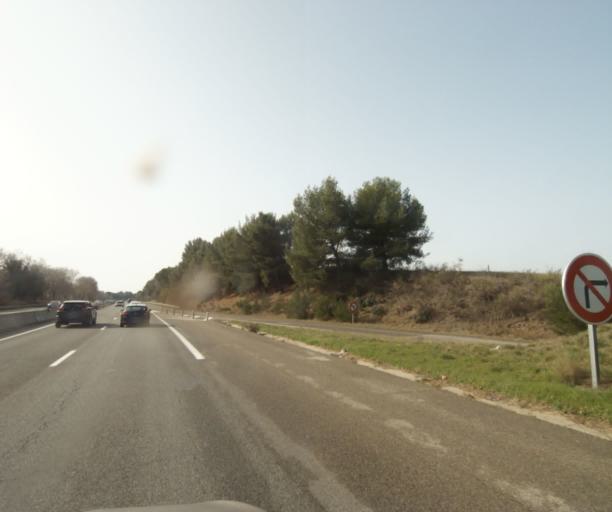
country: FR
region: Provence-Alpes-Cote d'Azur
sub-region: Departement des Bouches-du-Rhone
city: Venelles
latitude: 43.5717
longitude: 5.4676
